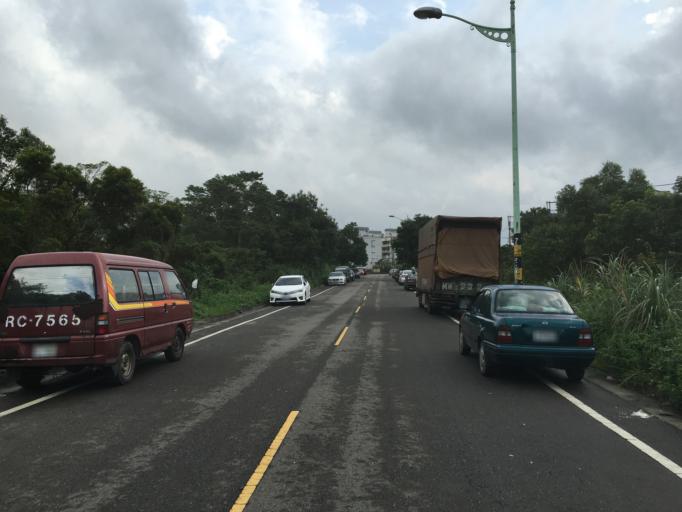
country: TW
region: Taiwan
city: Daxi
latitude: 24.8702
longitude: 121.2310
